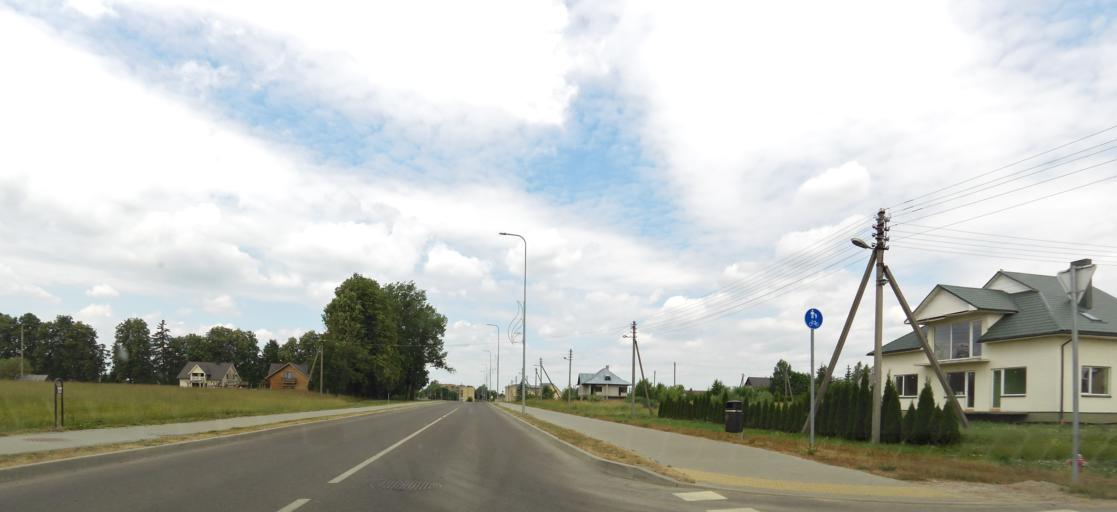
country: LT
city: Sirvintos
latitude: 55.0439
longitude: 24.9647
